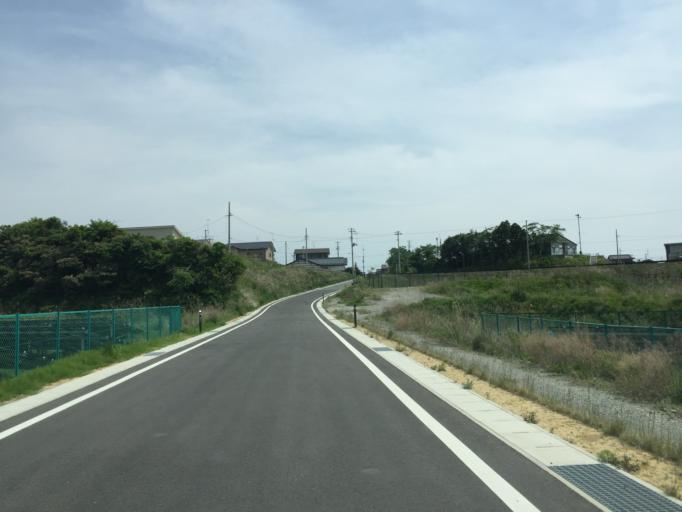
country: JP
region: Miyagi
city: Marumori
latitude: 37.8276
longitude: 140.9557
